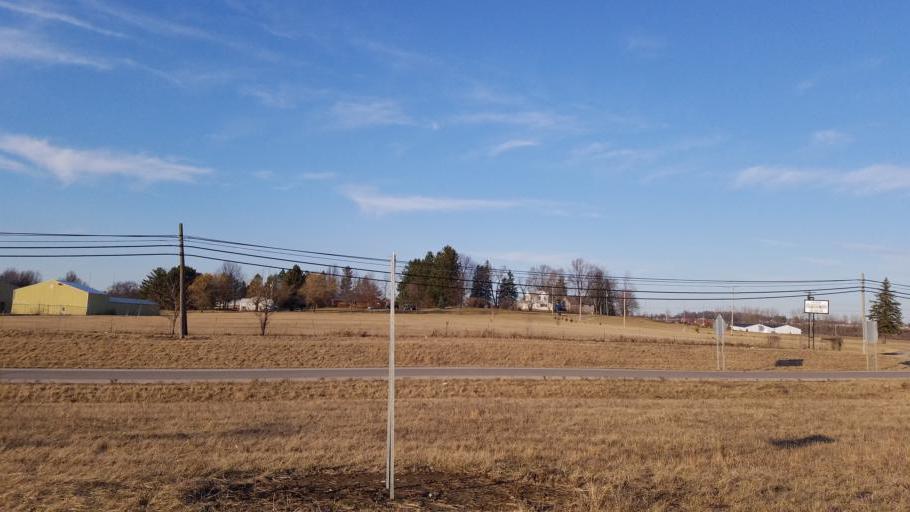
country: US
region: Ohio
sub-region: Richland County
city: Ontario
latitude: 40.7600
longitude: -82.6144
